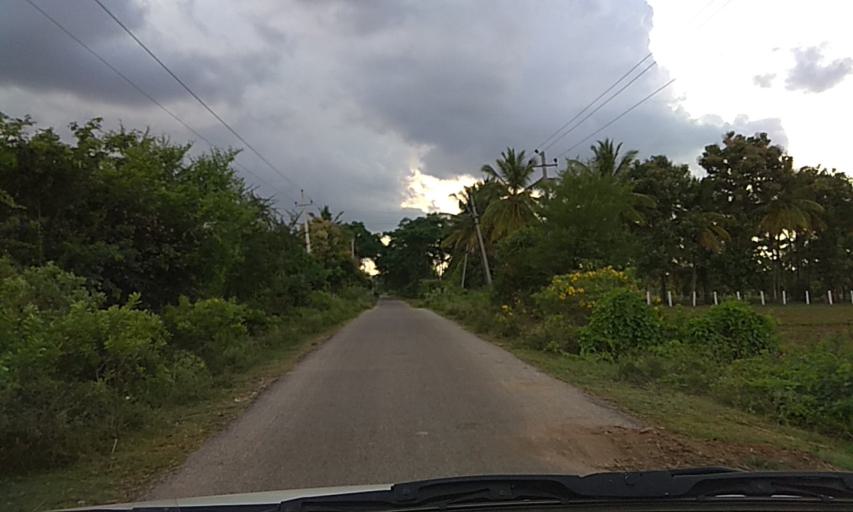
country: IN
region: Karnataka
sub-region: Chamrajnagar
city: Gundlupet
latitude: 11.8714
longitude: 76.7440
